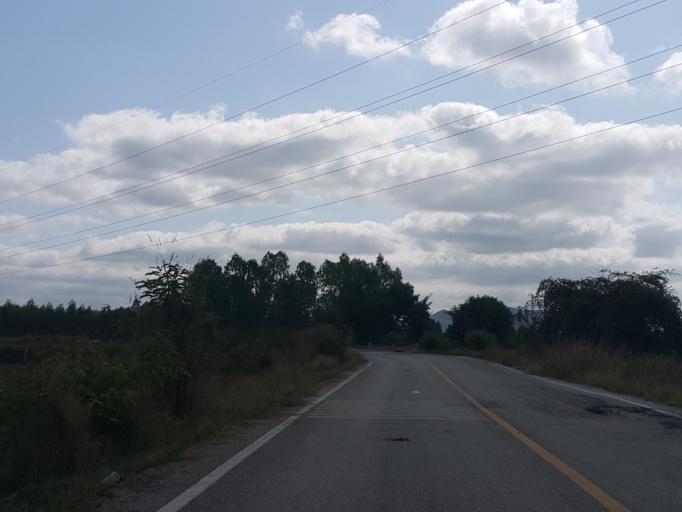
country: TH
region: Lamphun
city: Lamphun
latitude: 18.5455
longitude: 99.0860
